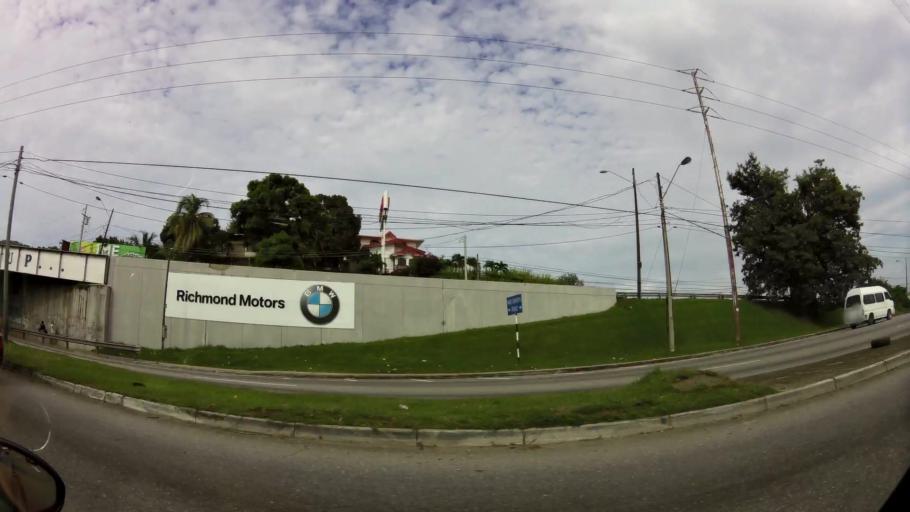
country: TT
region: City of Port of Spain
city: Mucurapo
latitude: 10.6742
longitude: -61.5417
